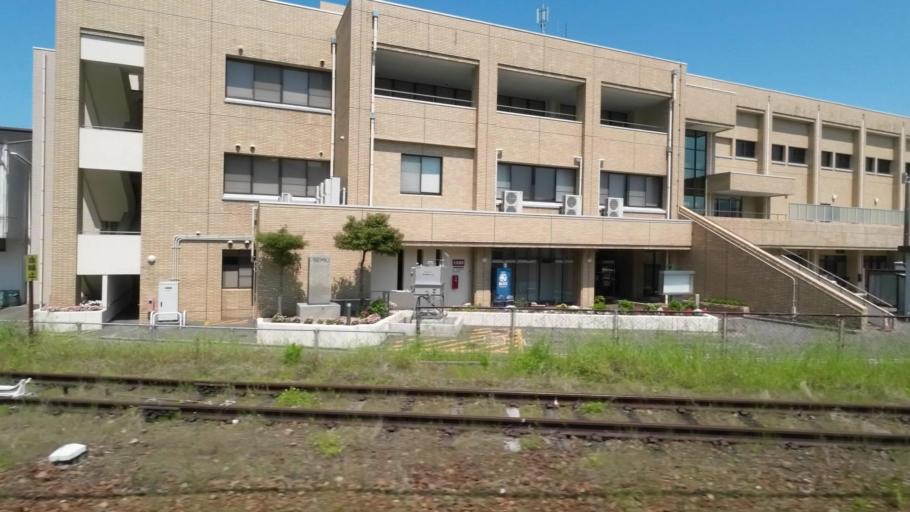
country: JP
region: Ehime
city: Hojo
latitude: 34.0337
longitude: 132.8421
